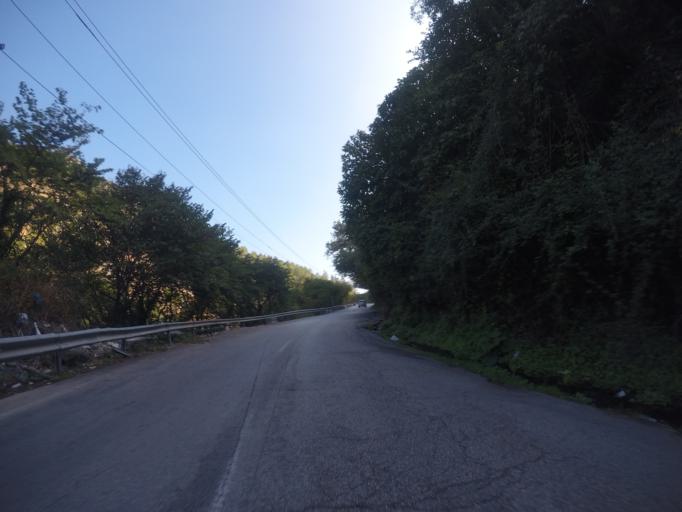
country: AL
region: Vlore
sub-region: Rrethi i Delvines
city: Mesopotam
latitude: 39.9187
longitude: 20.1411
